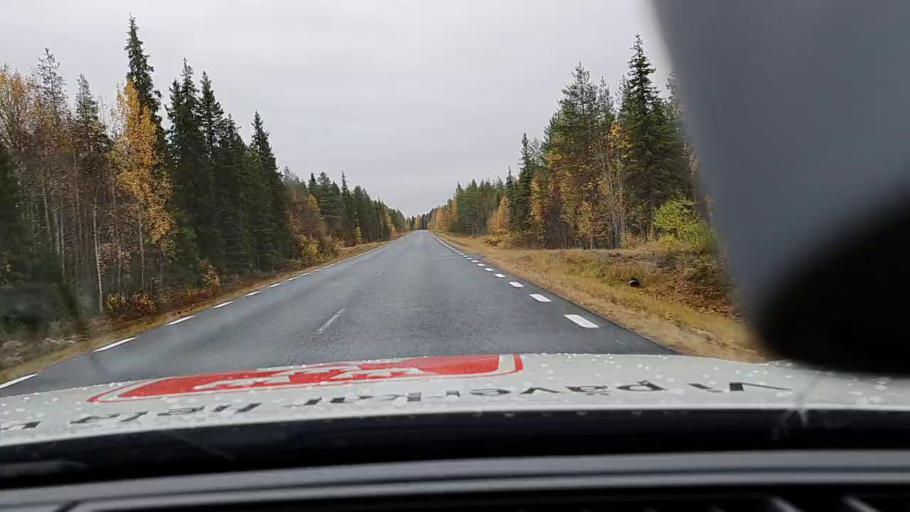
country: FI
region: Lapland
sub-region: Torniolaakso
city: Ylitornio
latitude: 66.1543
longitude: 23.8737
